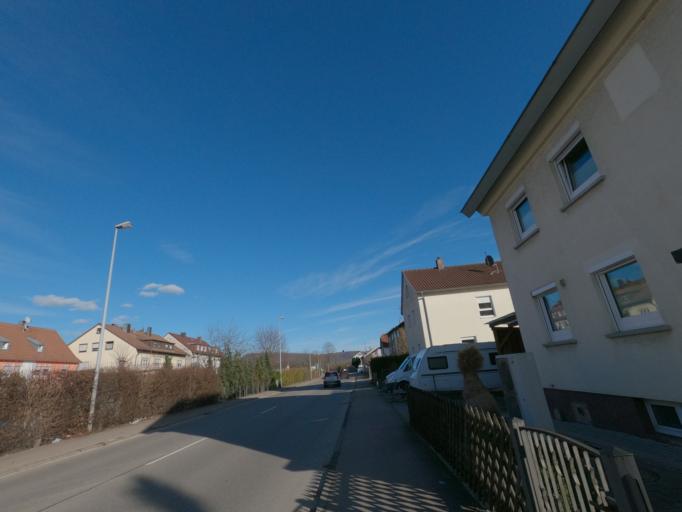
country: DE
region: Baden-Wuerttemberg
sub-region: Regierungsbezirk Stuttgart
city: Sussen
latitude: 48.6832
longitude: 9.7652
